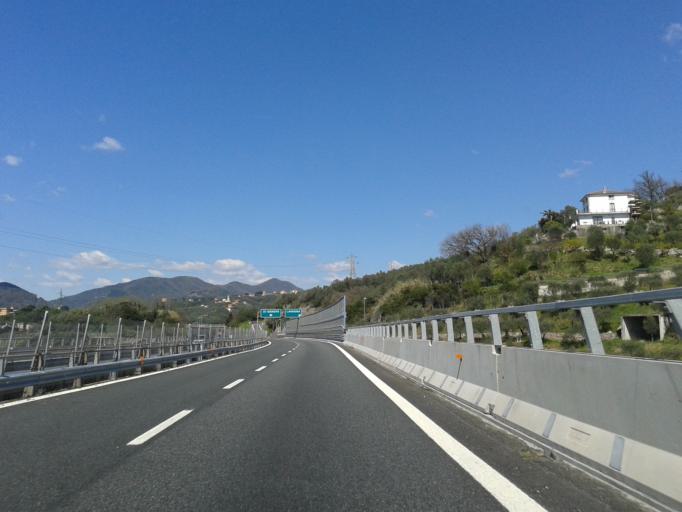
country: IT
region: Liguria
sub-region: Provincia di Genova
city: Lavagna
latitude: 44.3153
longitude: 9.3547
